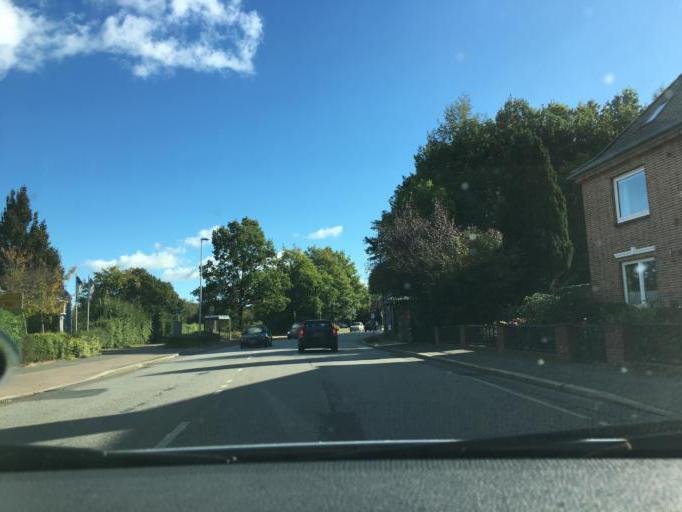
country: DE
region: Schleswig-Holstein
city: Kronshagen
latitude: 54.3290
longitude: 10.0943
